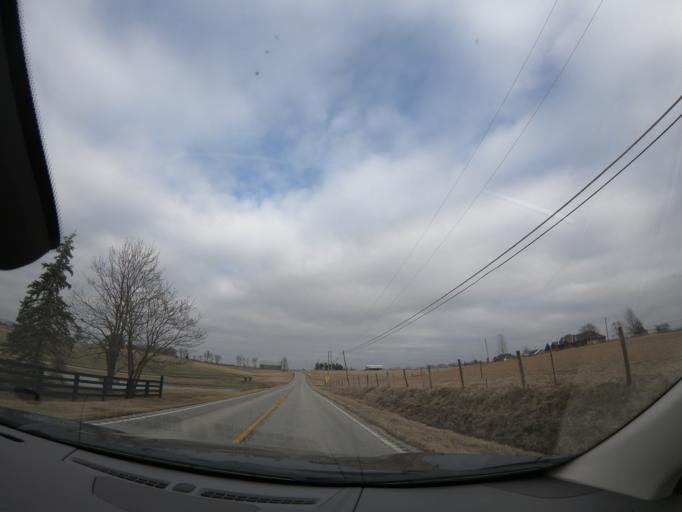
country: US
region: Kentucky
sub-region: Spencer County
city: Taylorsville
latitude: 37.8728
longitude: -85.3141
